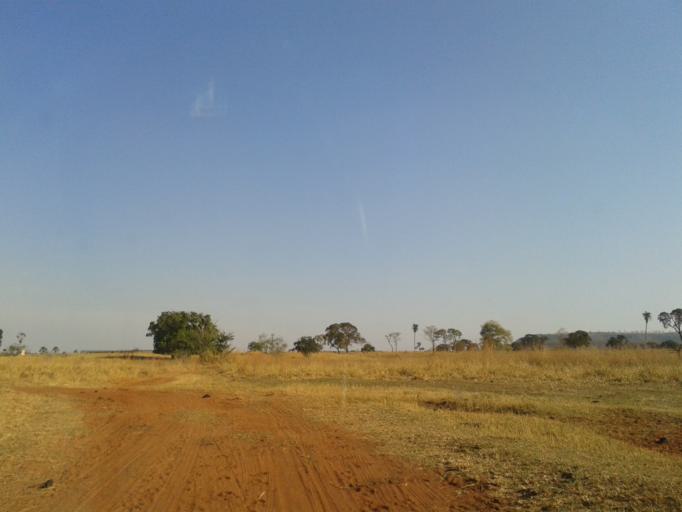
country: BR
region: Minas Gerais
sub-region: Santa Vitoria
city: Santa Vitoria
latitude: -19.1624
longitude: -50.0208
